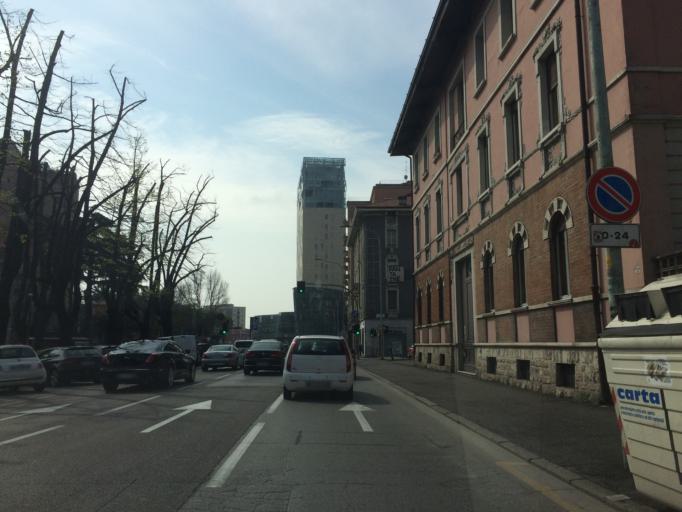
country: IT
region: Lombardy
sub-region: Provincia di Brescia
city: Brescia
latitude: 45.5382
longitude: 10.2098
